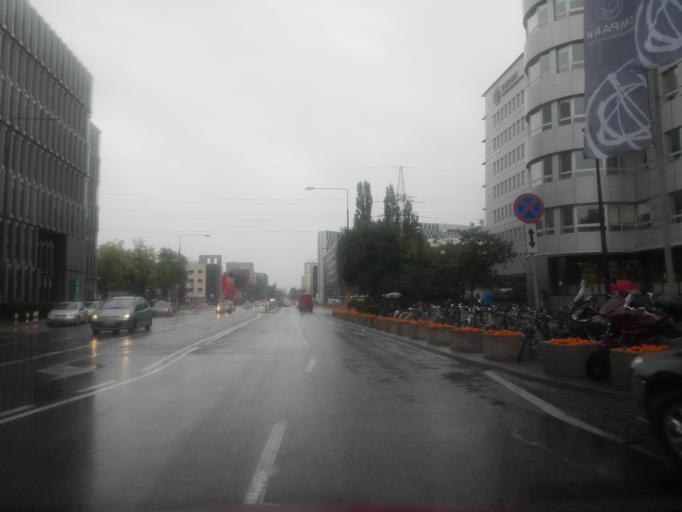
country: PL
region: Masovian Voivodeship
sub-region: Warszawa
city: Mokotow
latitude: 52.1832
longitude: 20.9997
